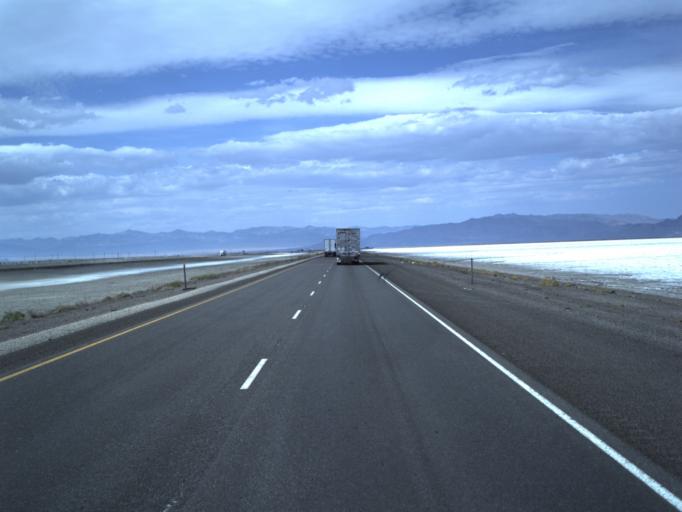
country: US
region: Utah
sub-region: Tooele County
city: Wendover
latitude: 40.7384
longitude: -113.8016
